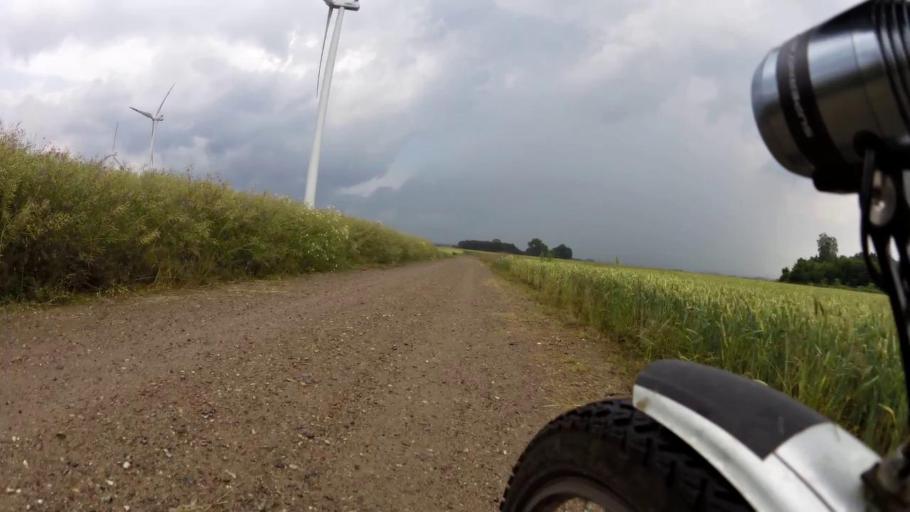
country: PL
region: West Pomeranian Voivodeship
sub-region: Powiat lobeski
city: Lobez
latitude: 53.7127
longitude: 15.6347
